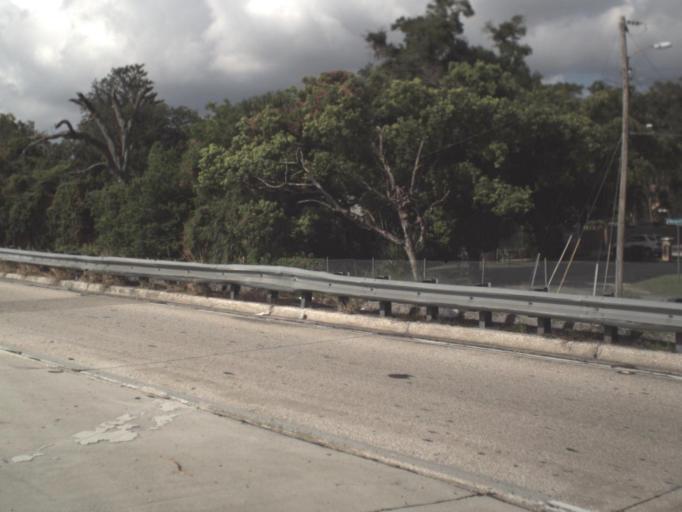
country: US
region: Florida
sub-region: Hillsborough County
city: Tampa
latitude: 27.9791
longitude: -82.4539
